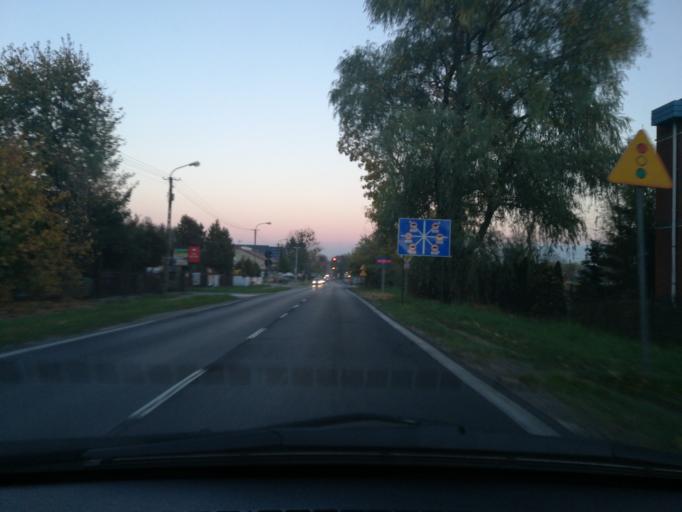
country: PL
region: Lodz Voivodeship
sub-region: Powiat lodzki wschodni
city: Andrespol
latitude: 51.7940
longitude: 19.5873
